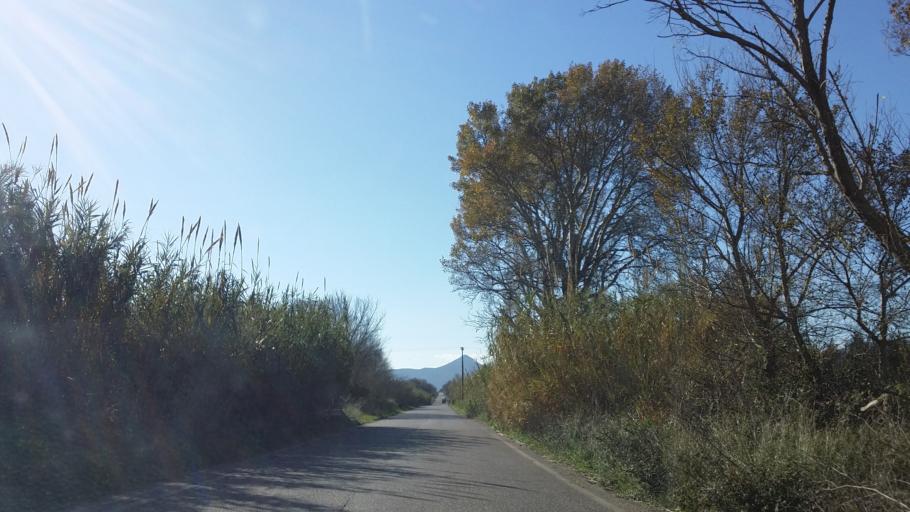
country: GR
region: West Greece
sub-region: Nomos Aitolias kai Akarnanias
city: Vonitsa
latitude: 38.8612
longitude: 20.8786
